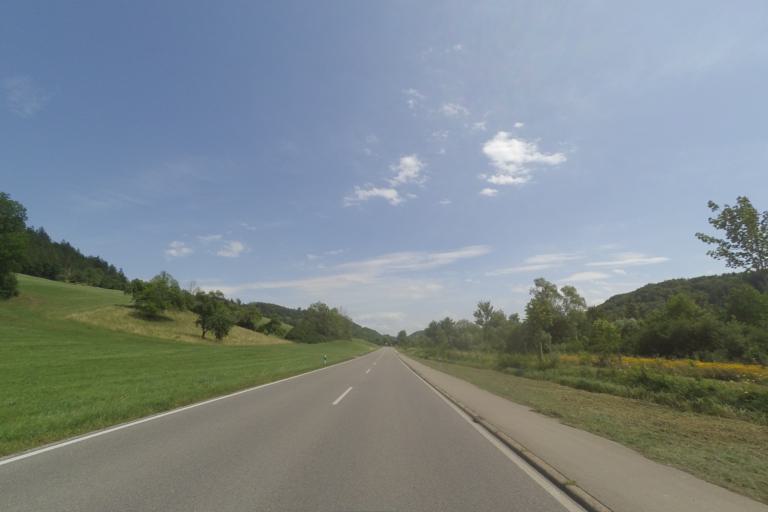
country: DE
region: Baden-Wuerttemberg
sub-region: Regierungsbezirk Stuttgart
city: Gaildorf
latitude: 48.9757
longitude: 9.8089
